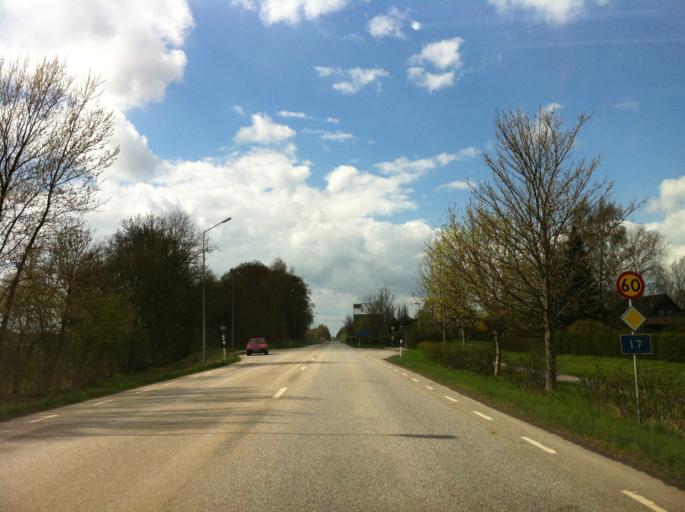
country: SE
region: Skane
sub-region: Eslovs Kommun
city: Stehag
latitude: 55.8512
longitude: 13.4138
